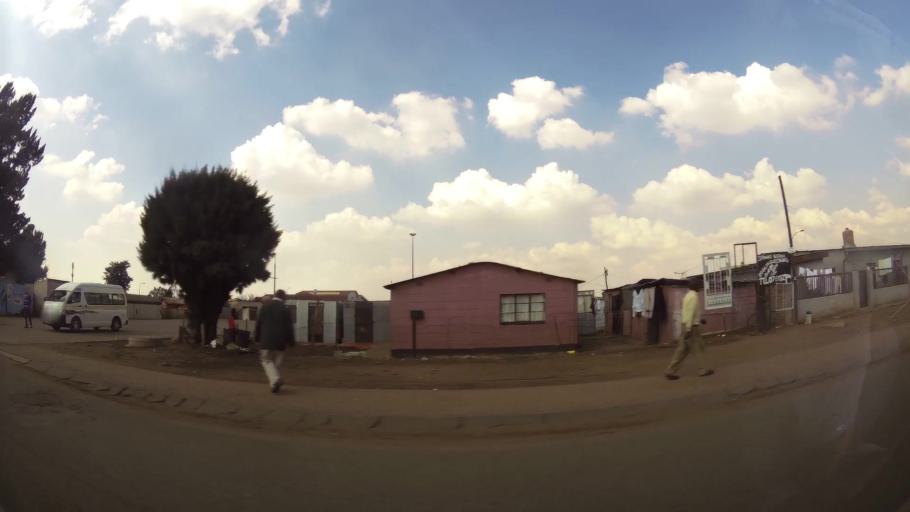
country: ZA
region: Gauteng
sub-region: Ekurhuleni Metropolitan Municipality
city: Germiston
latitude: -26.3378
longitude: 28.1406
